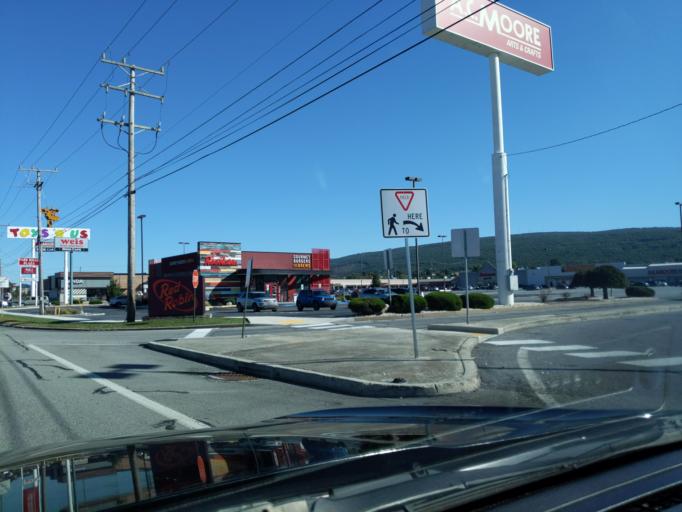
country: US
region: Pennsylvania
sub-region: Blair County
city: Lakemont
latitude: 40.4700
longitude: -78.4067
